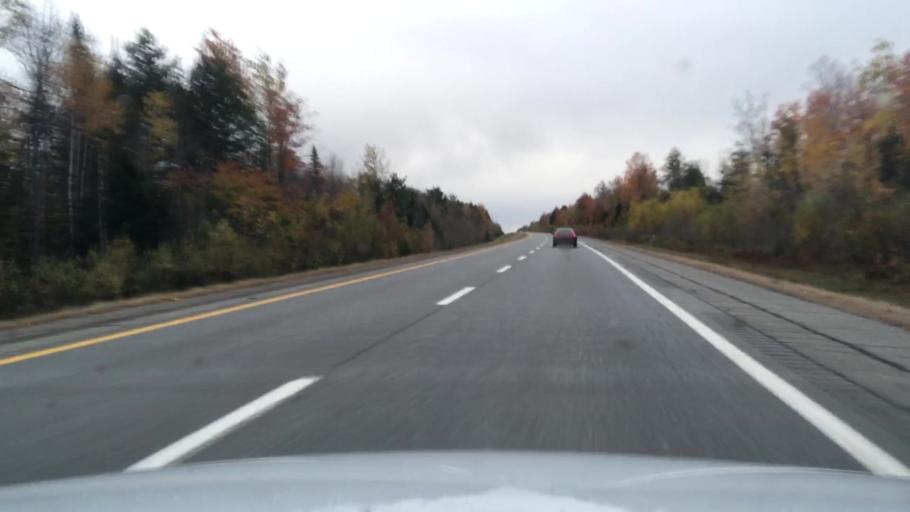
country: US
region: Maine
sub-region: Penobscot County
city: Greenbush
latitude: 45.0970
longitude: -68.6961
